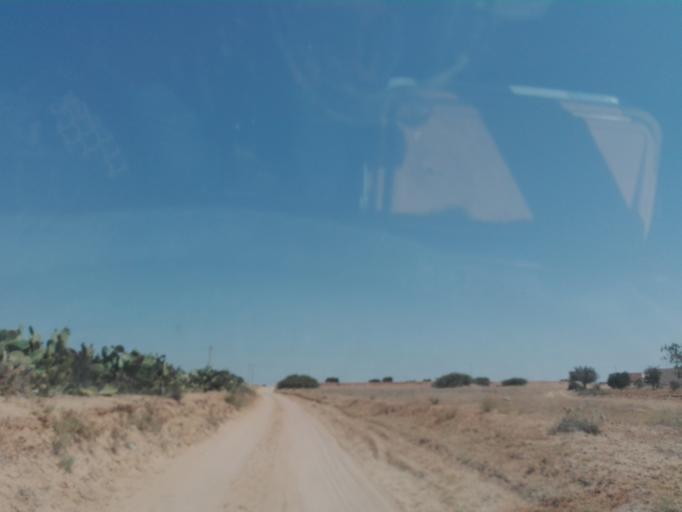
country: TN
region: Safaqis
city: Bi'r `Ali Bin Khalifah
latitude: 34.6721
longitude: 10.2345
